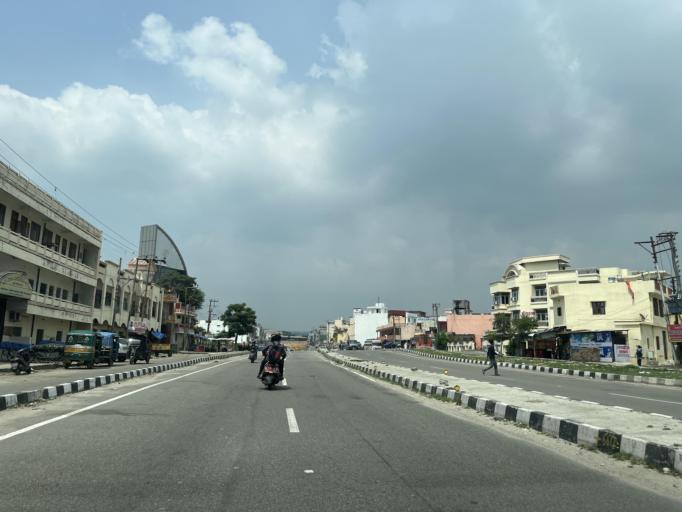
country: IN
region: Uttarakhand
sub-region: Haridwar
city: Haridwar
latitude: 29.9773
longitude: 78.1825
